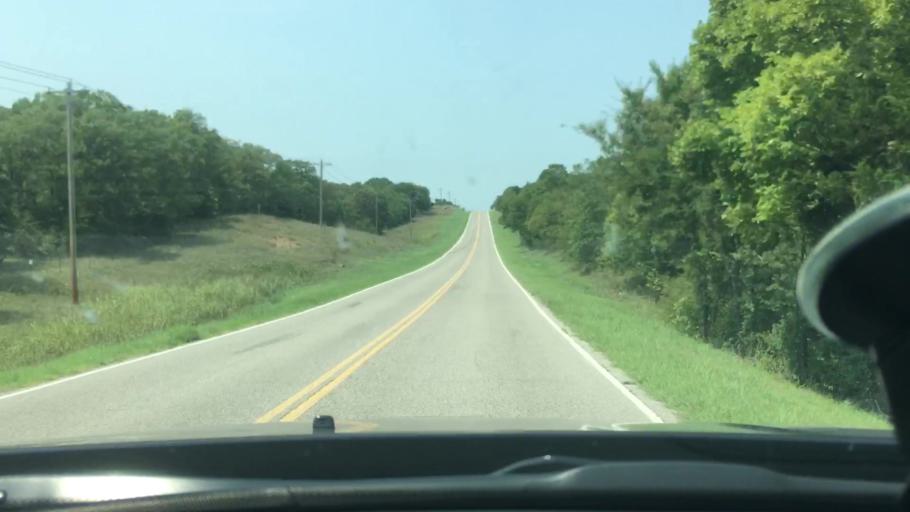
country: US
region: Oklahoma
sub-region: Love County
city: Marietta
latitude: 33.9714
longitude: -97.0059
